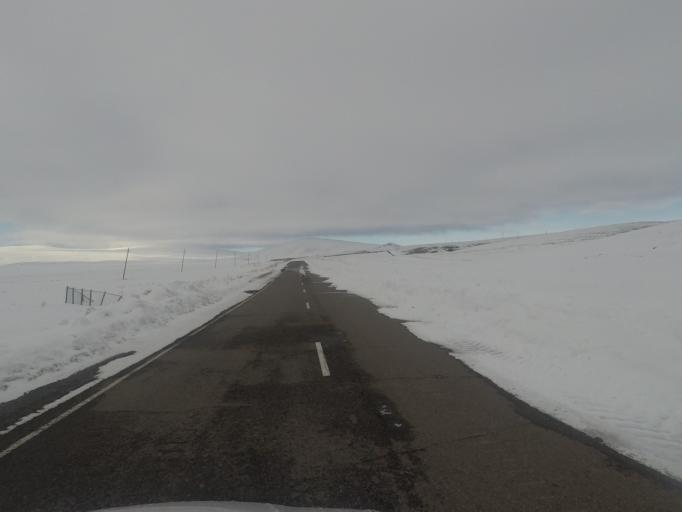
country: GE
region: Samtskhe-Javakheti
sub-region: Ninotsminda
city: Ninotsminda
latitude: 41.4249
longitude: 43.8349
